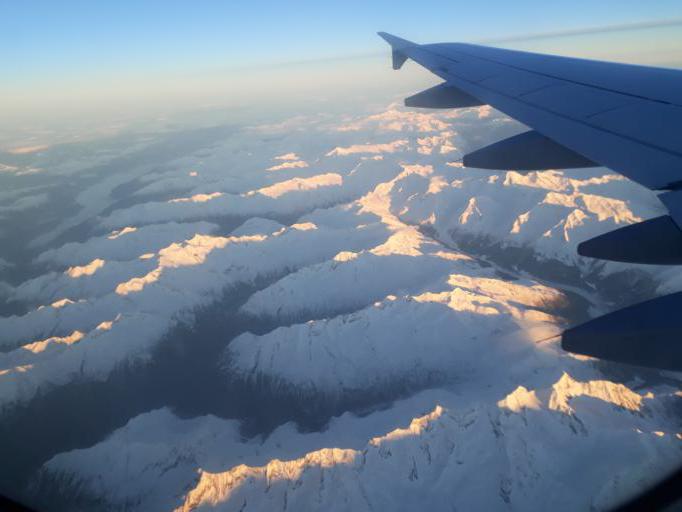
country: AT
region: Tyrol
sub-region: Politischer Bezirk Schwaz
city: Mayrhofen
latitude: 47.0719
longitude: 11.8685
